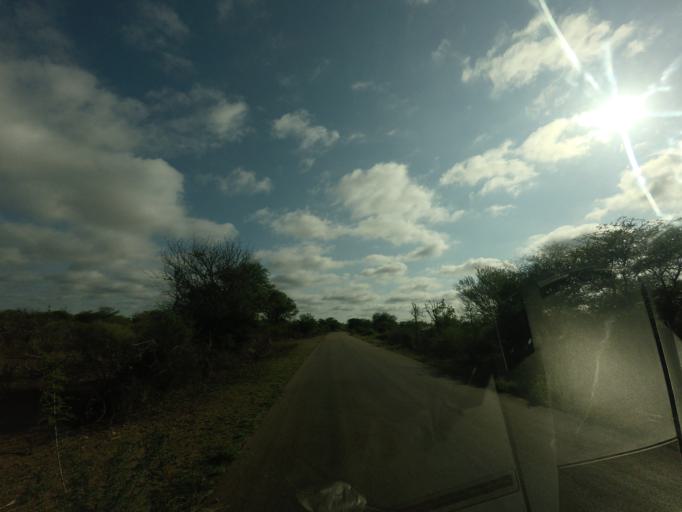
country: ZA
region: Mpumalanga
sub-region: Ehlanzeni District
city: Komatipoort
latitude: -25.2125
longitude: 31.8694
